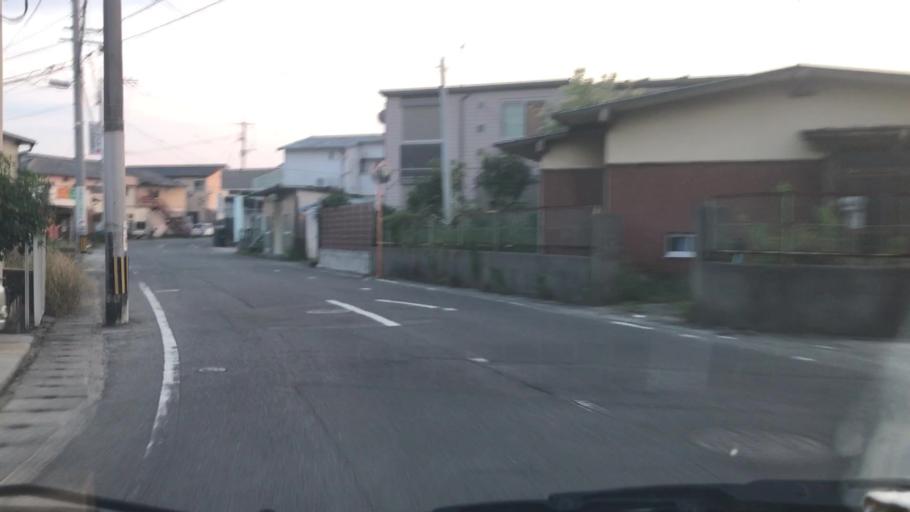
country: JP
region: Saga Prefecture
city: Saga-shi
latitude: 33.2568
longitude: 130.2894
